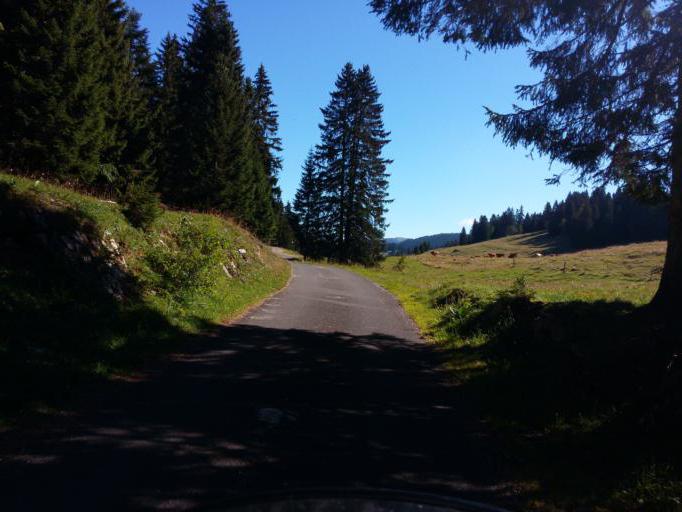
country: CH
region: Vaud
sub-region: Nyon District
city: Saint-George
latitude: 46.5271
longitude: 6.2092
